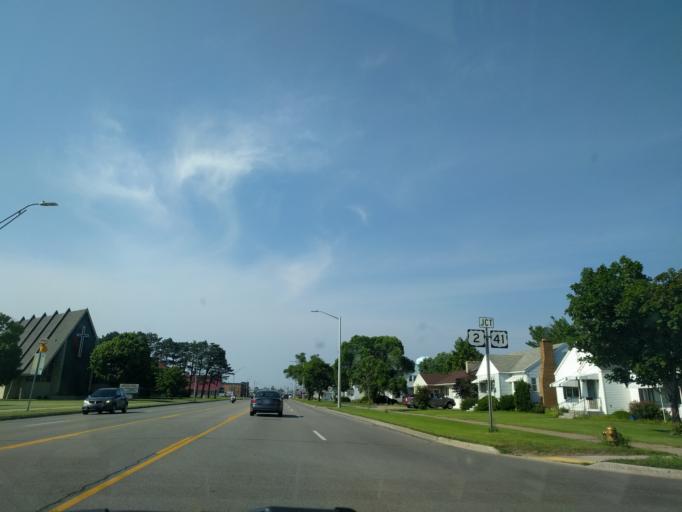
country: US
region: Michigan
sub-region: Delta County
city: Escanaba
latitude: 45.7422
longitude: -87.0798
